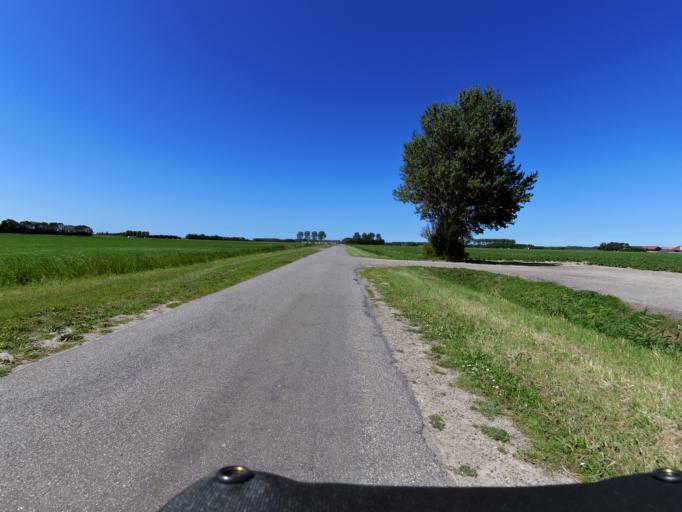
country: NL
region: South Holland
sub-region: Gemeente Goeree-Overflakkee
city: Dirksland
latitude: 51.7893
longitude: 4.0457
